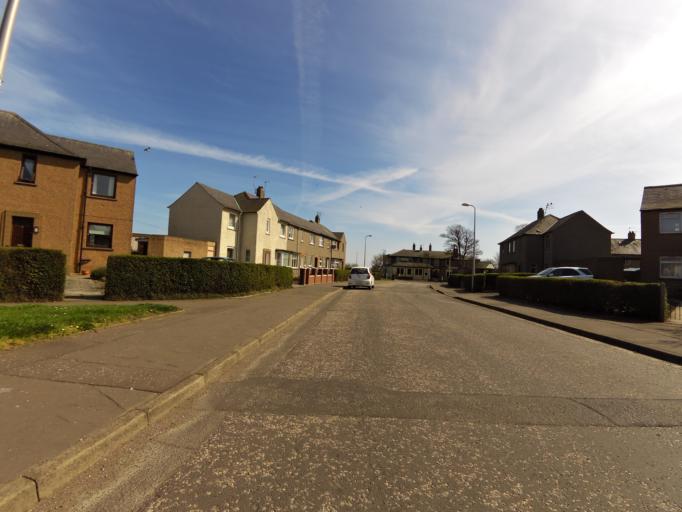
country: GB
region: Scotland
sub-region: Angus
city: Arbroath
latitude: 56.5648
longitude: -2.5657
